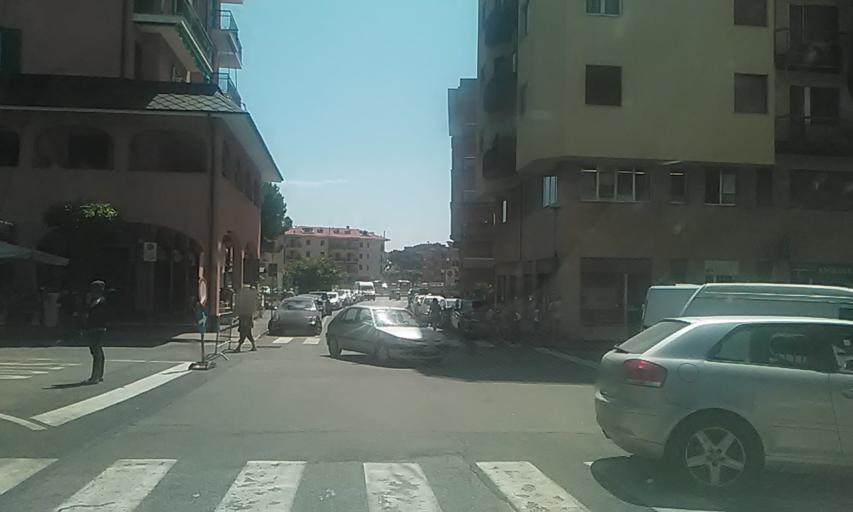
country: IT
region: Liguria
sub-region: Provincia di Savona
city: Andora
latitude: 43.9500
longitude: 8.1410
